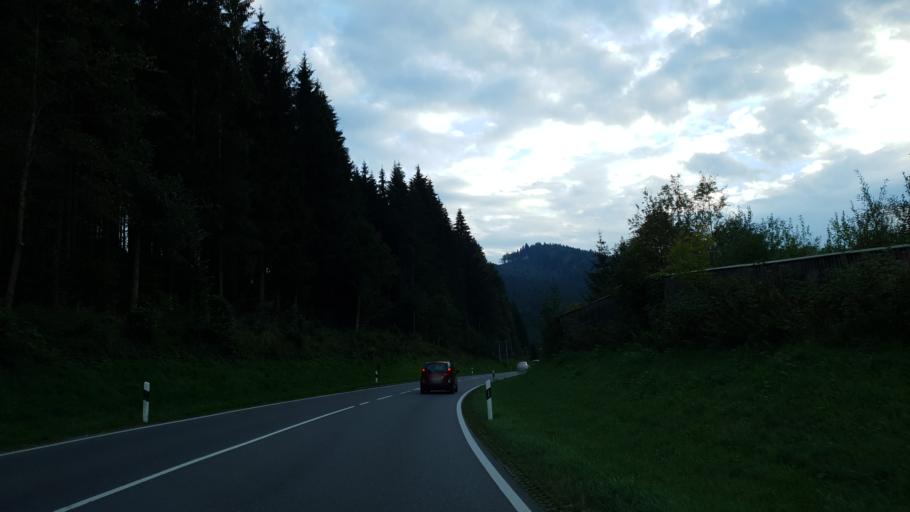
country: DE
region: Bavaria
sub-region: Swabia
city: Maierhofen
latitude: 47.6551
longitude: 10.0885
